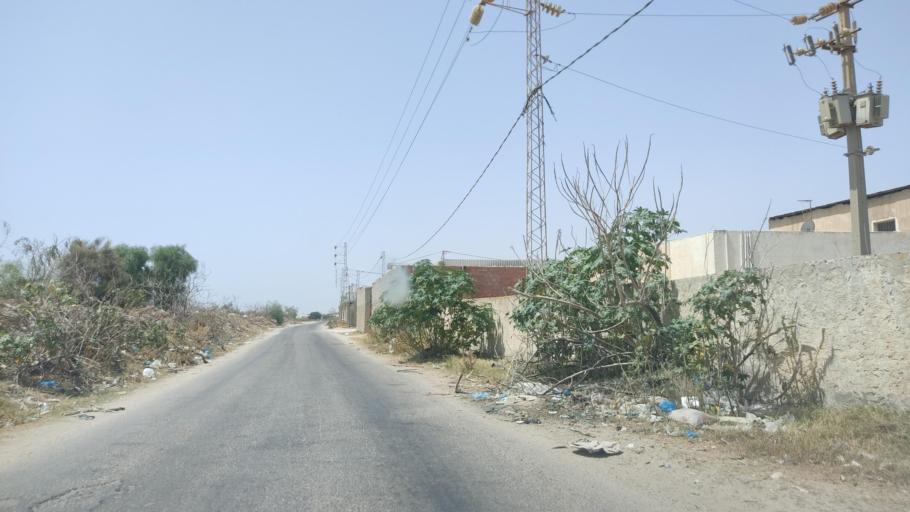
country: TN
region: Safaqis
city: Sfax
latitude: 34.7073
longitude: 10.7199
